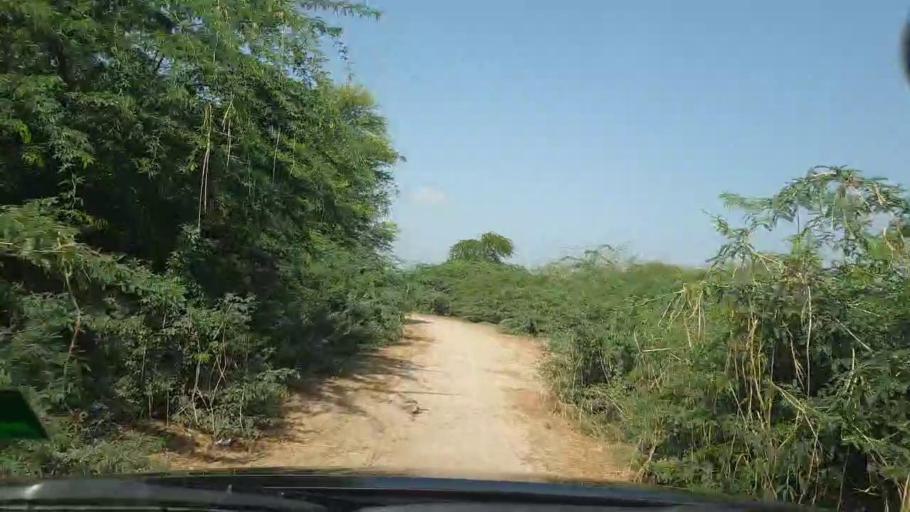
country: PK
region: Sindh
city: Tando Bago
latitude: 24.7732
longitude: 68.9462
